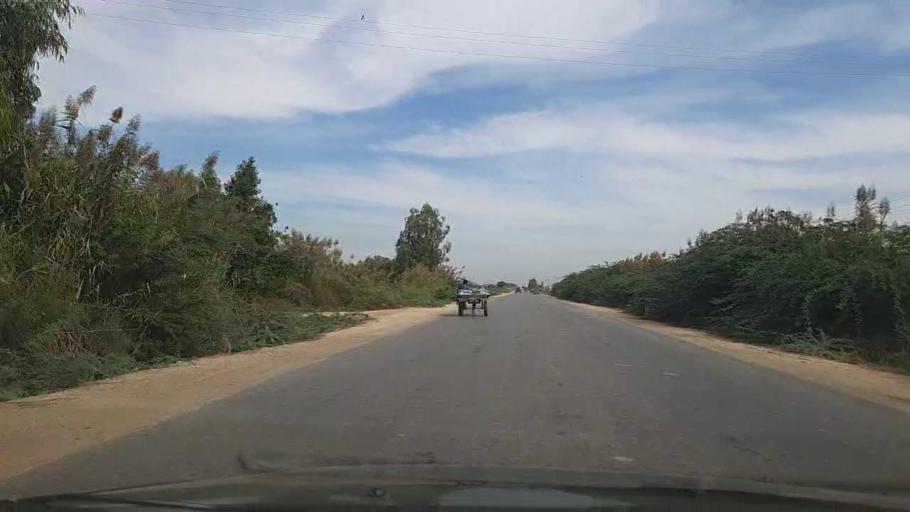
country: PK
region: Sindh
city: Thatta
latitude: 24.7600
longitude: 67.9320
